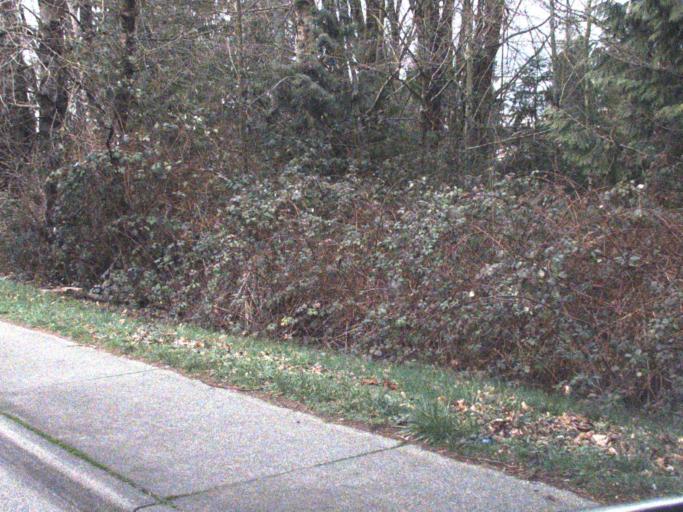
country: US
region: Washington
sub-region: Snohomish County
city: Marysville
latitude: 48.0526
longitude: -122.1618
